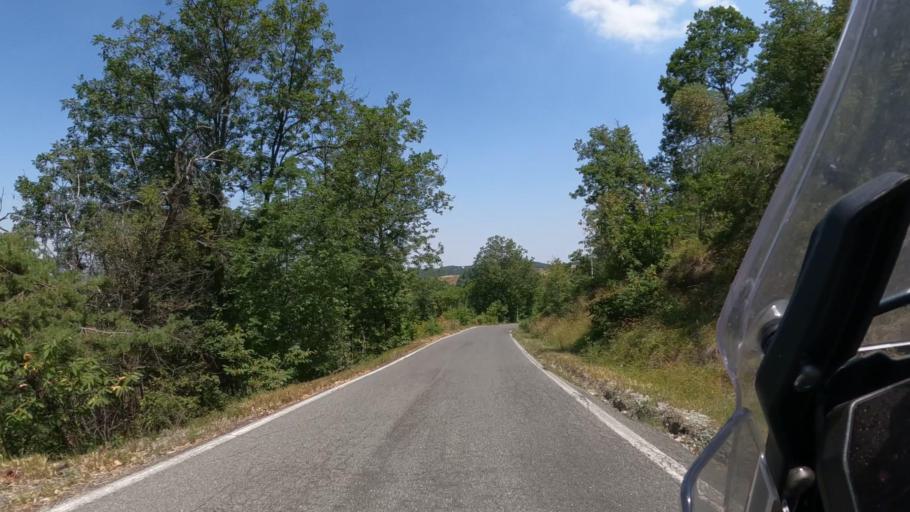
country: IT
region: Piedmont
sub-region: Provincia di Alessandria
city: Morbello
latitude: 44.5557
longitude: 8.5057
